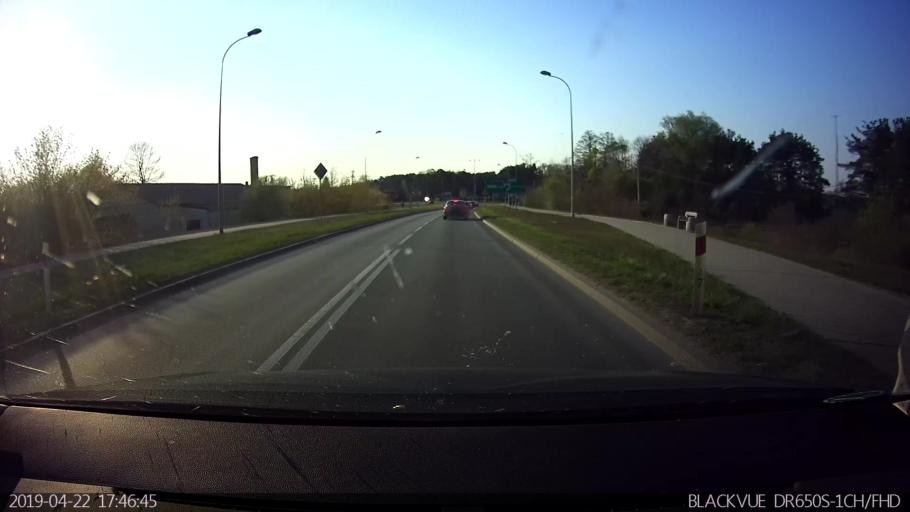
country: PL
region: Masovian Voivodeship
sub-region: Powiat wegrowski
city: Wegrow
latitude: 52.4029
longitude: 22.0245
